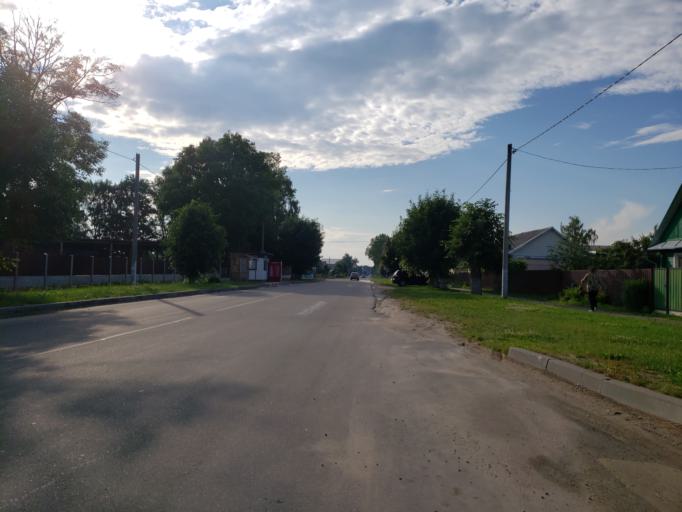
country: BY
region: Minsk
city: Chervyen'
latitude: 53.7031
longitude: 28.4403
